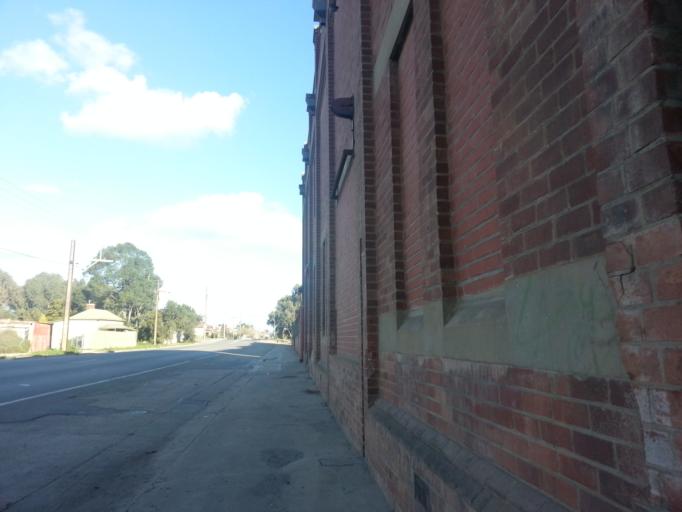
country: AU
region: South Australia
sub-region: Port Adelaide Enfield
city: Alberton
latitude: -34.8466
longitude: 138.5165
